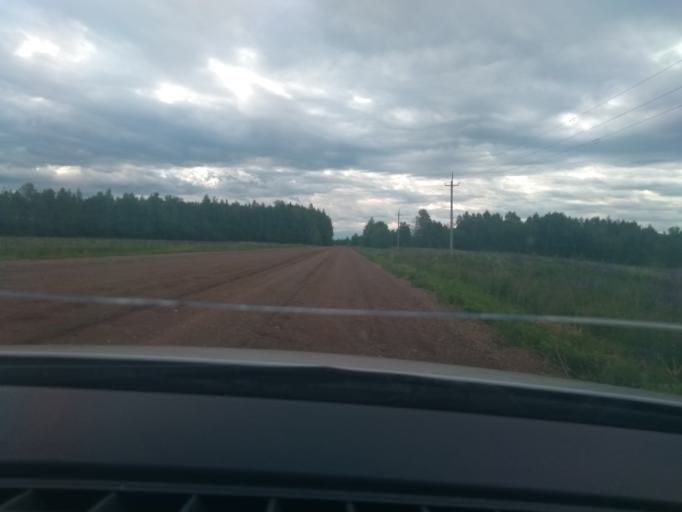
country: RU
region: Perm
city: Sylva
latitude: 57.8184
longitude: 56.7205
